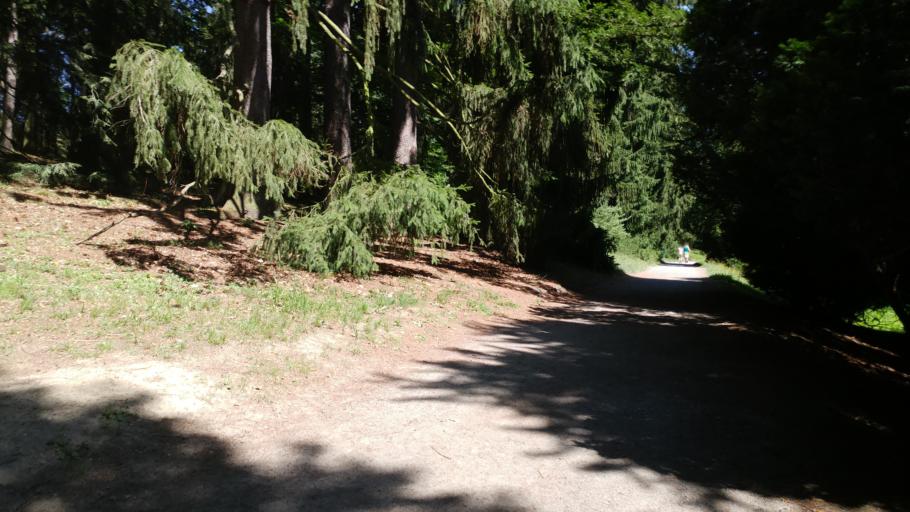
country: CZ
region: Central Bohemia
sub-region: Okres Praha-Zapad
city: Pruhonice
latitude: 49.9966
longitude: 14.5571
